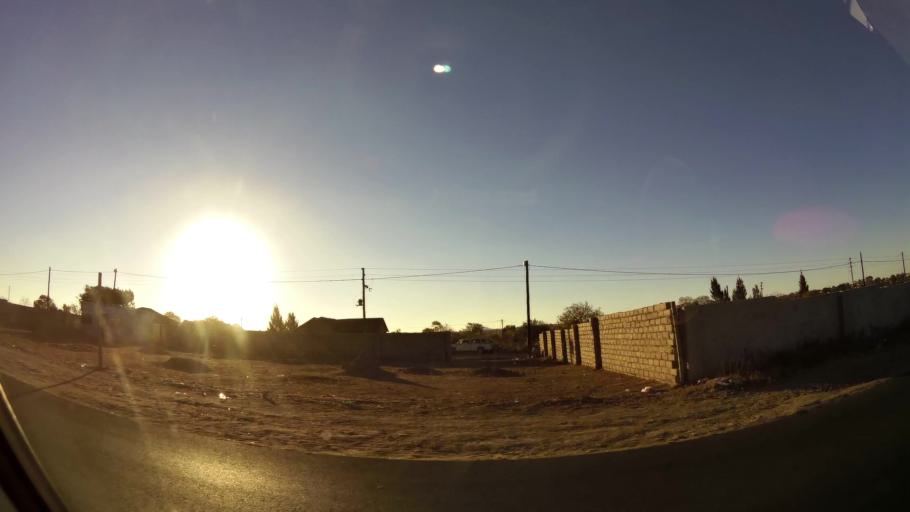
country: ZA
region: Limpopo
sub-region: Capricorn District Municipality
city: Polokwane
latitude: -23.8310
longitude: 29.3726
